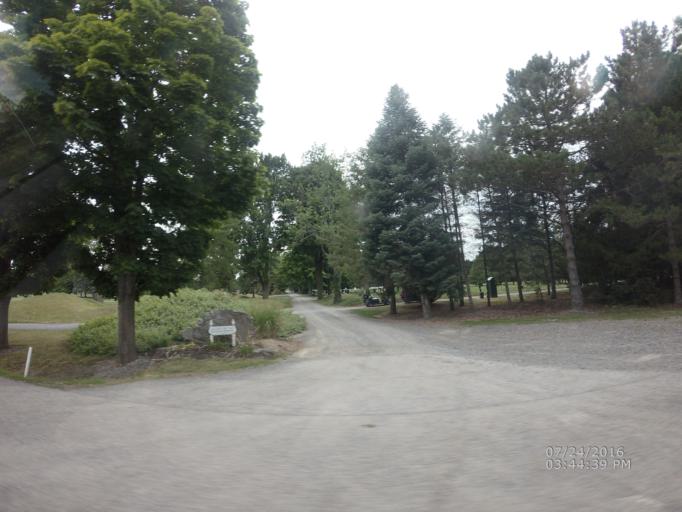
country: US
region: New York
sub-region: Onondaga County
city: Camillus
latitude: 43.0168
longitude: -76.3049
